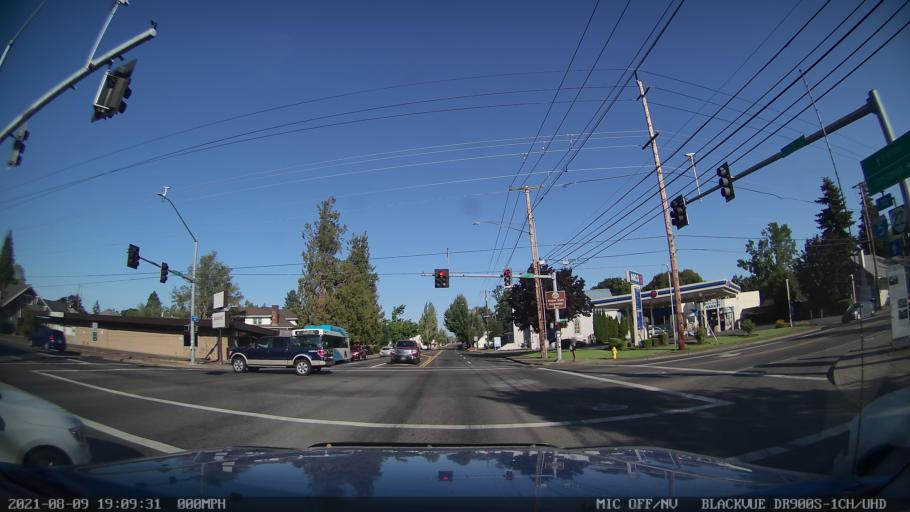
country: US
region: Oregon
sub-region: Marion County
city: Salem
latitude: 44.9352
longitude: -123.0205
